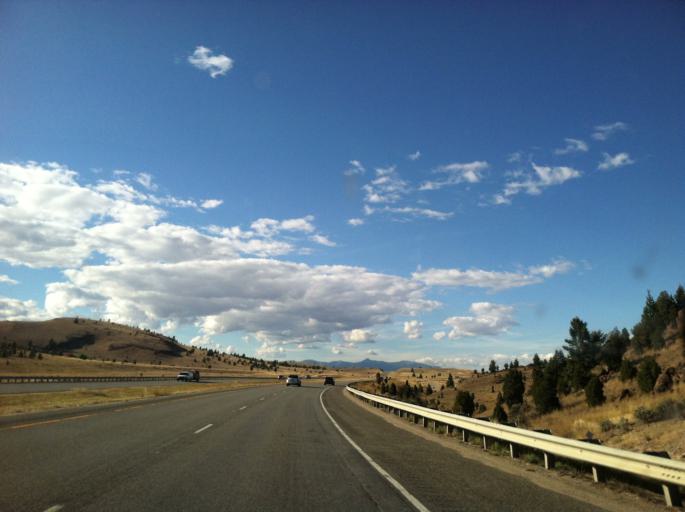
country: US
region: Montana
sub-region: Silver Bow County
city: Butte-Silver Bow (Balance)
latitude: 46.0235
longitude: -112.7269
